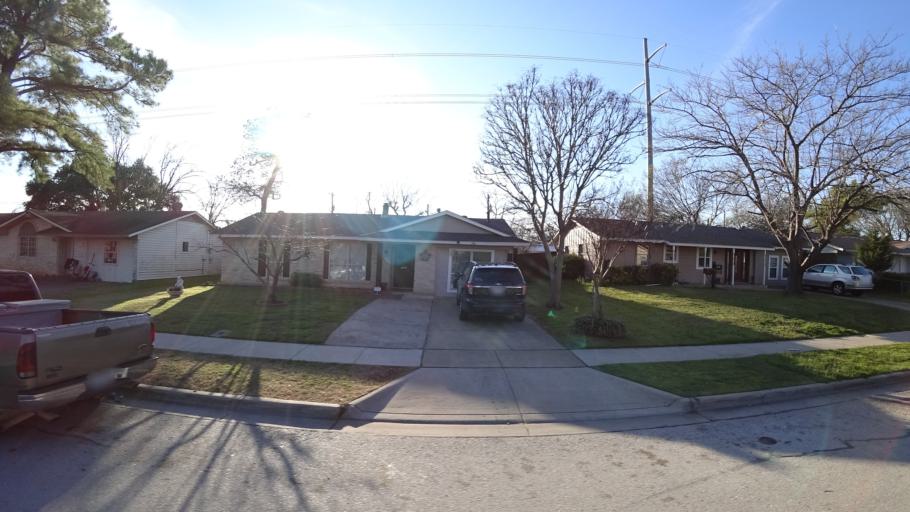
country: US
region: Texas
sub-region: Denton County
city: Lewisville
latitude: 33.0400
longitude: -97.0096
